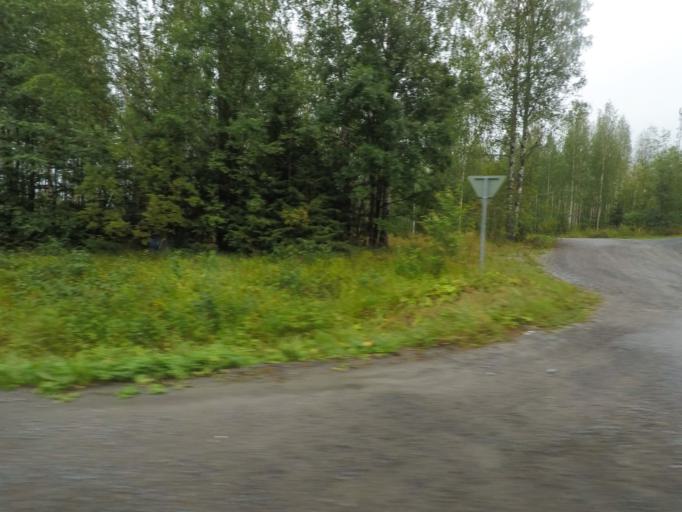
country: FI
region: Southern Savonia
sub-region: Pieksaemaeki
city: Joroinen
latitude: 62.1206
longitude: 27.8389
